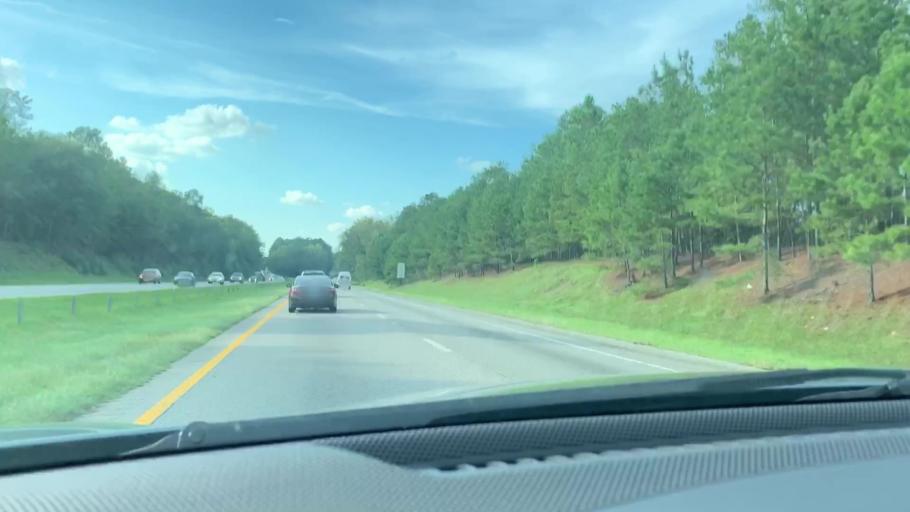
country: US
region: South Carolina
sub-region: Orangeburg County
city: Brookdale
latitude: 33.4633
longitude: -80.7363
